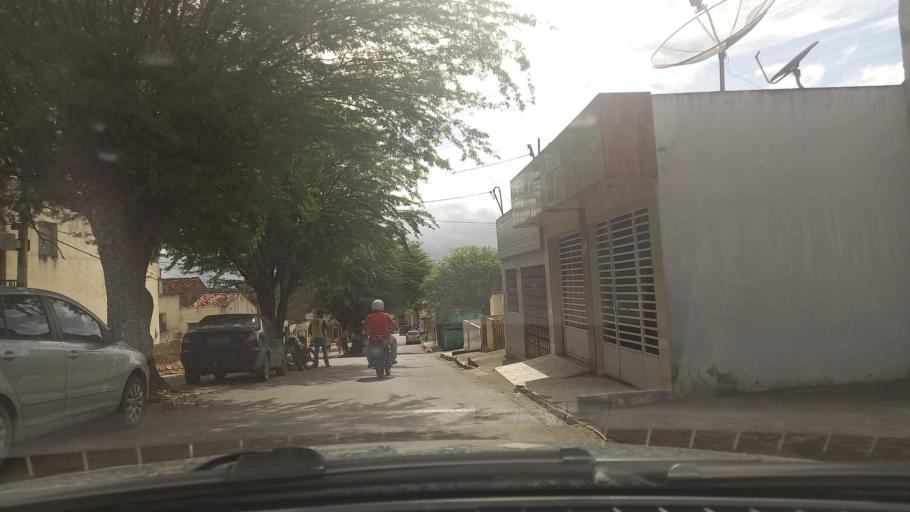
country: BR
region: Pernambuco
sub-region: Vitoria De Santo Antao
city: Vitoria de Santo Antao
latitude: -8.1231
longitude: -35.2911
